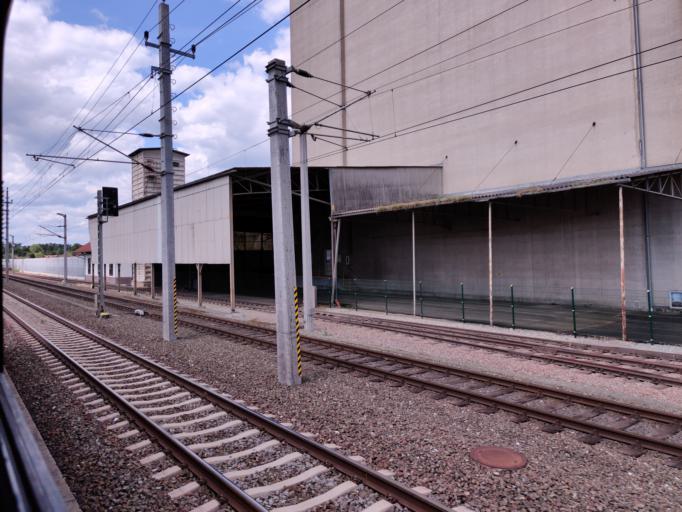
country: AT
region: Styria
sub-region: Politischer Bezirk Graz-Umgebung
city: Kalsdorf bei Graz
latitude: 46.9663
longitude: 15.4689
